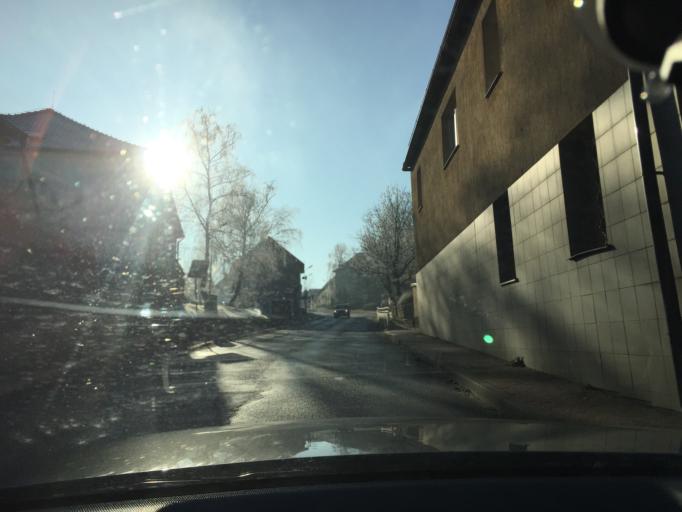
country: CZ
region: Central Bohemia
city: Trebotov
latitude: 50.0225
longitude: 14.2974
